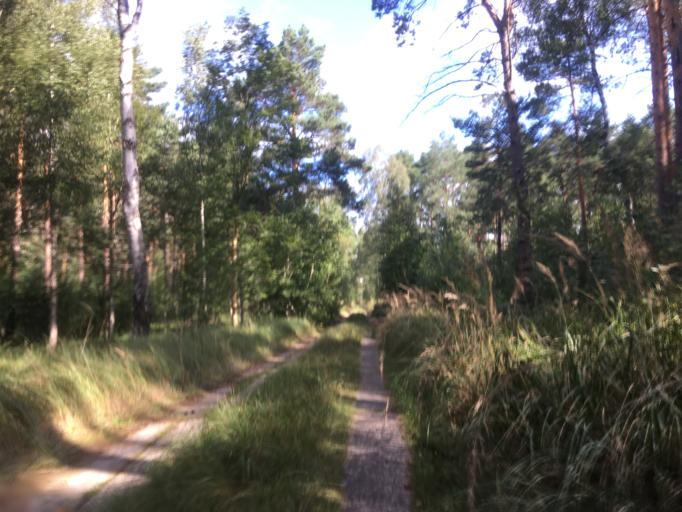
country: DE
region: Brandenburg
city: Halbe
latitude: 52.1651
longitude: 13.7484
